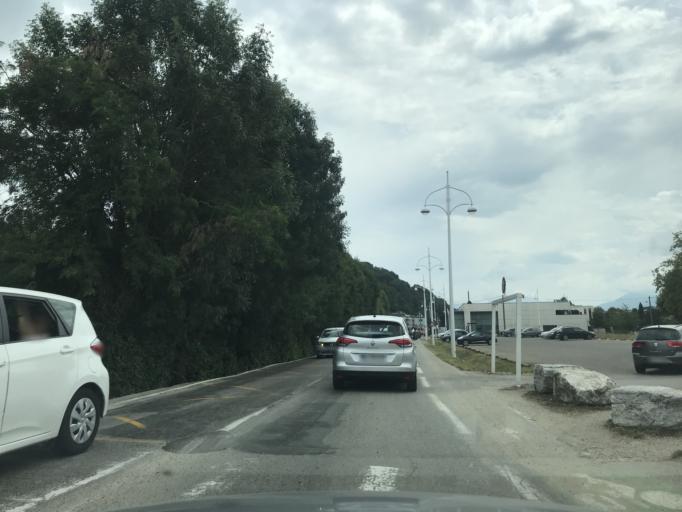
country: FR
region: Rhone-Alpes
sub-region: Departement de la Savoie
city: Tresserve
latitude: 45.6956
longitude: 5.8960
